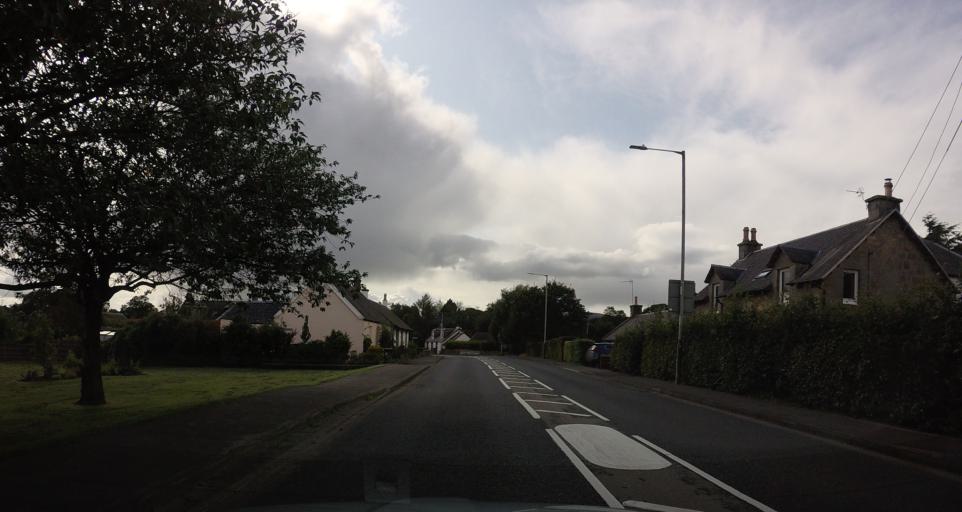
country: GB
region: Scotland
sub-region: Fife
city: Saline
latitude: 56.1846
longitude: -3.5580
